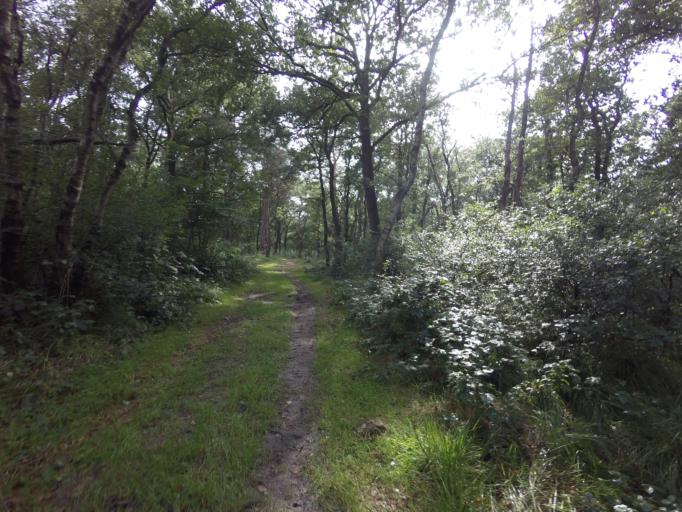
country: NL
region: Friesland
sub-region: Gemeente Heerenveen
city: Jubbega
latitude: 52.9628
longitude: 6.1408
